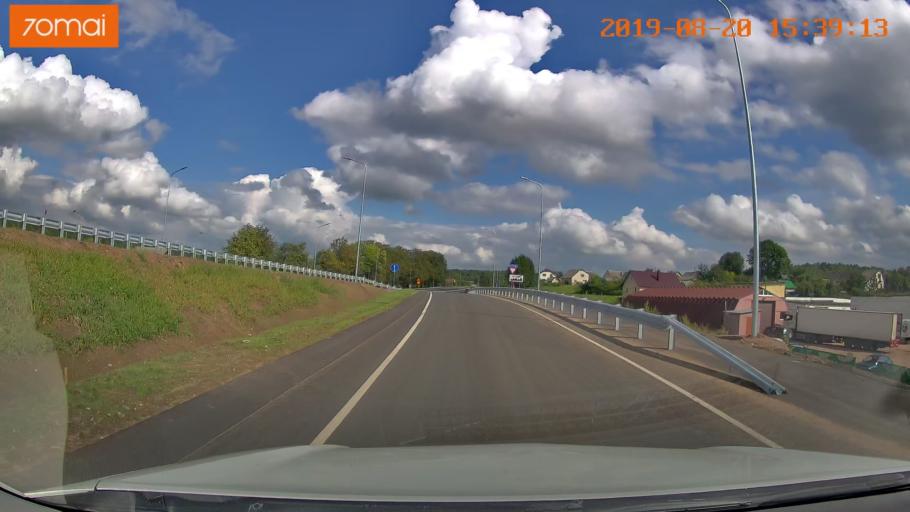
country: BY
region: Minsk
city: Astrashytski Haradok
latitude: 54.0548
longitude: 27.7511
